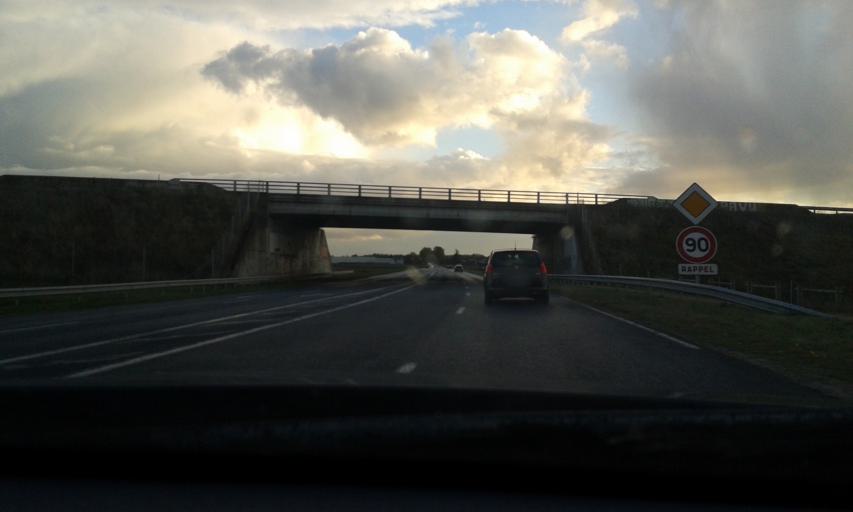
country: FR
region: Centre
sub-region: Departement du Loiret
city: Chevilly
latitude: 48.0455
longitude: 1.8743
